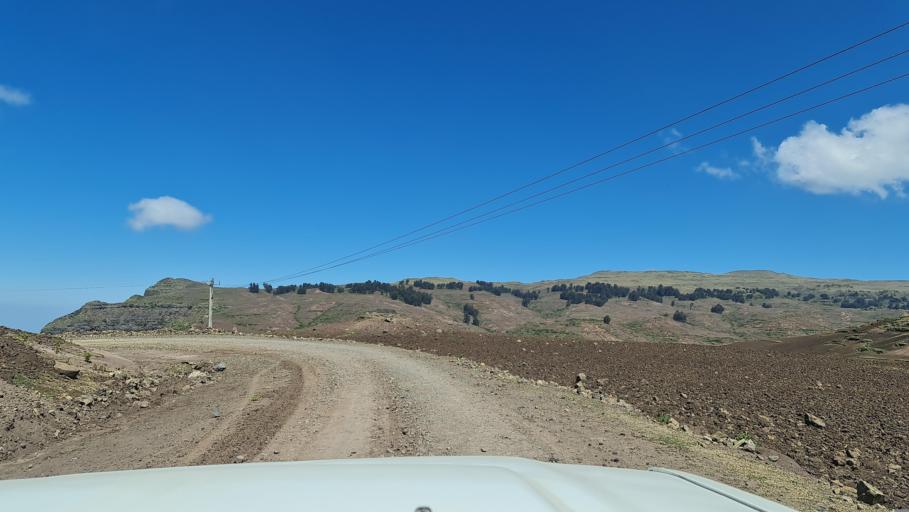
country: ET
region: Amhara
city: Debark'
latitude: 13.2354
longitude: 38.0810
